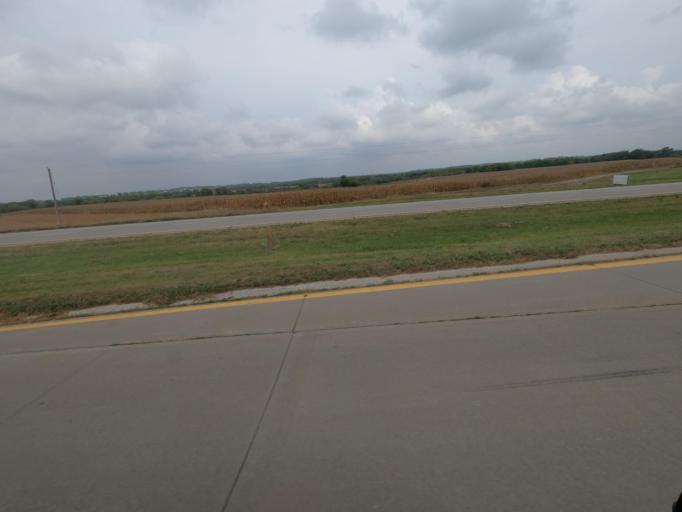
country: US
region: Iowa
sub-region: Wapello County
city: Eddyville
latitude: 41.1261
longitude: -92.5639
